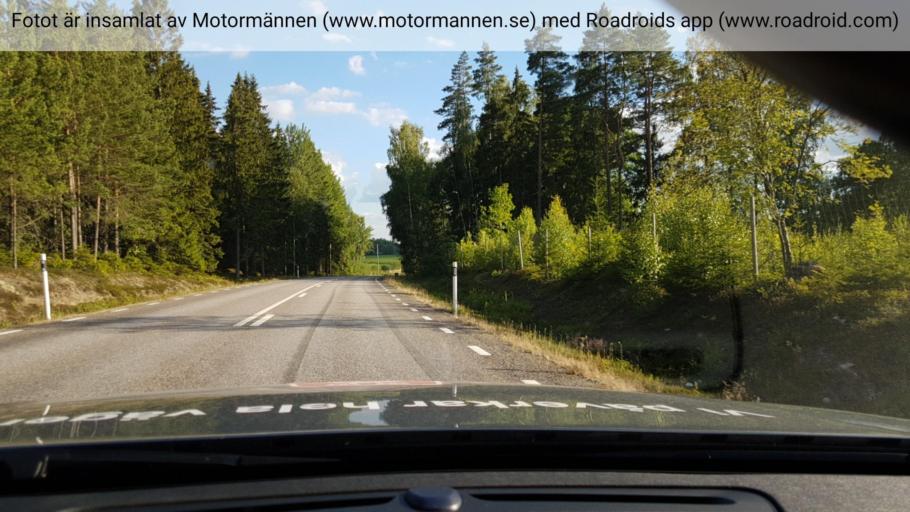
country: SE
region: Uppsala
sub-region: Heby Kommun
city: Morgongava
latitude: 59.8531
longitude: 16.9298
